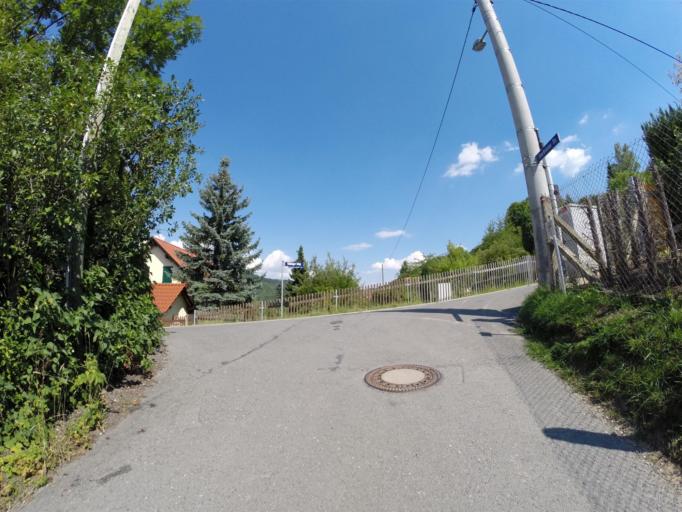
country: DE
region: Thuringia
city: Jena
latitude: 50.9187
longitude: 11.6055
